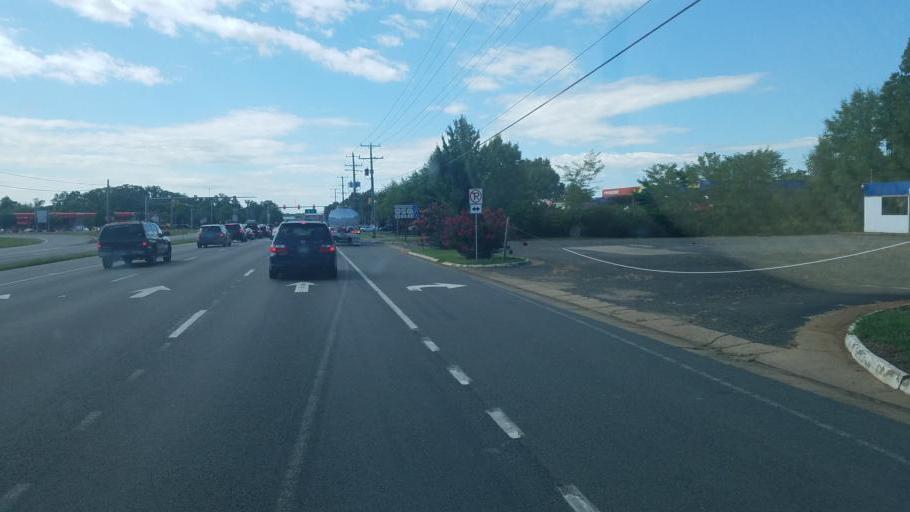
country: US
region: Virginia
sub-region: Fauquier County
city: Bealeton
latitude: 38.6223
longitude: -77.8008
